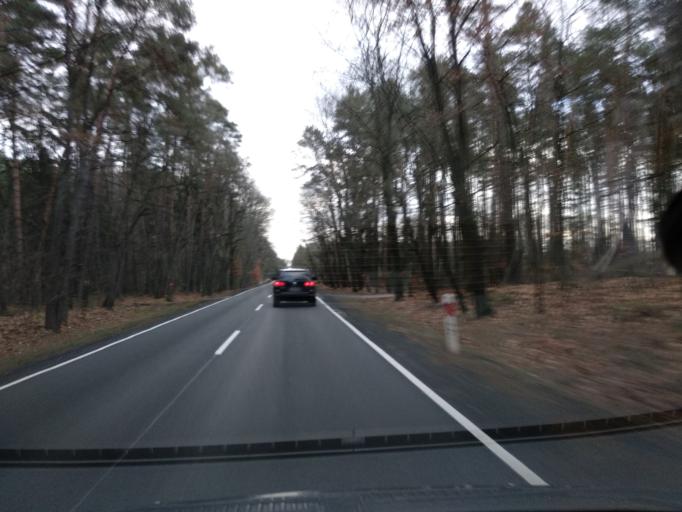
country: PL
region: Lower Silesian Voivodeship
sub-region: Powiat olesnicki
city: Miedzyborz
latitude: 51.4708
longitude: 17.7419
